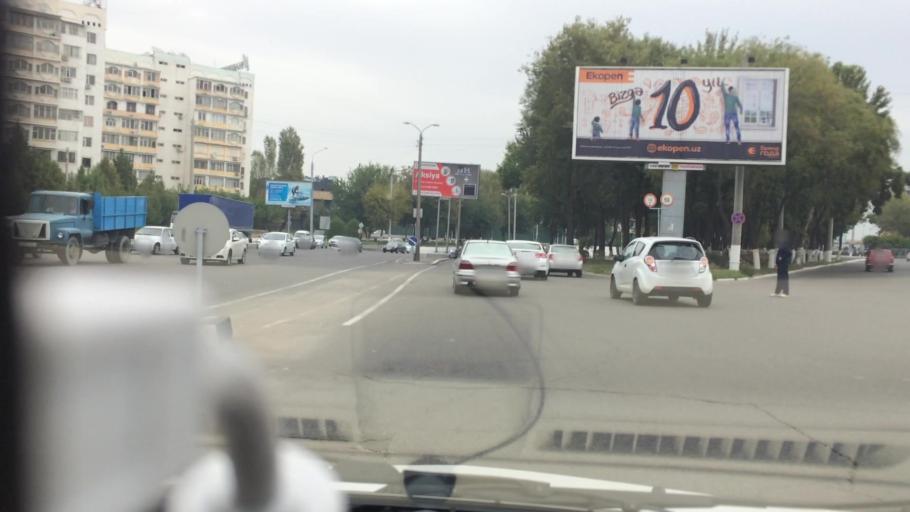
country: UZ
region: Toshkent Shahri
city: Tashkent
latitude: 41.2893
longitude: 69.2824
